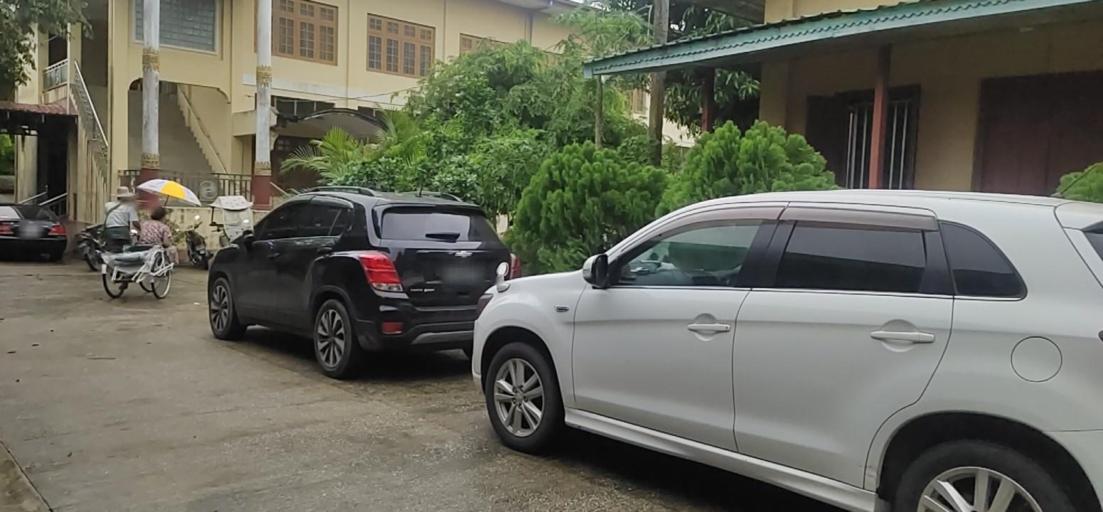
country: MM
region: Ayeyarwady
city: Pathein
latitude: 16.6054
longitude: 94.9224
